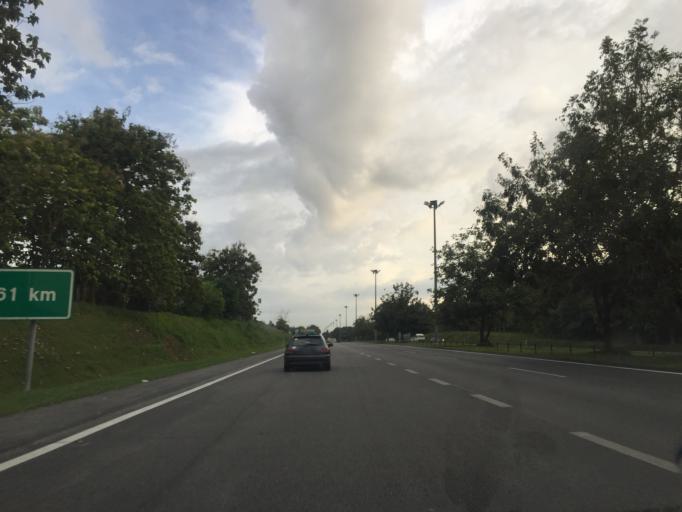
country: MY
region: Kedah
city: Gurun
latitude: 5.8265
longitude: 100.4892
